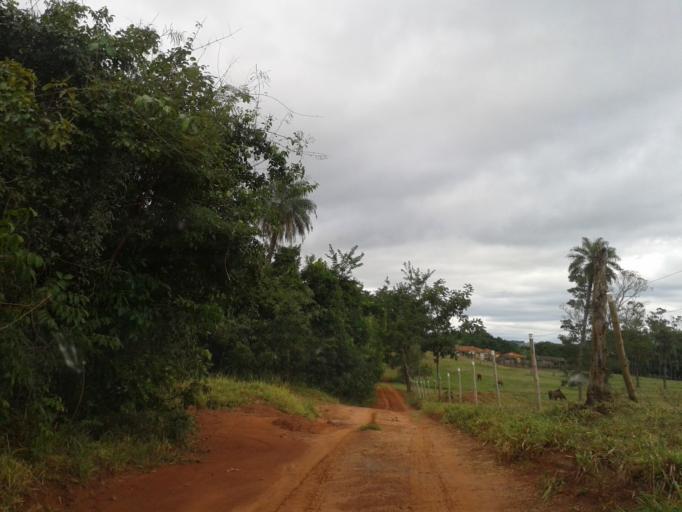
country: BR
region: Minas Gerais
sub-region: Campina Verde
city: Campina Verde
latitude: -19.4844
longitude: -49.6181
